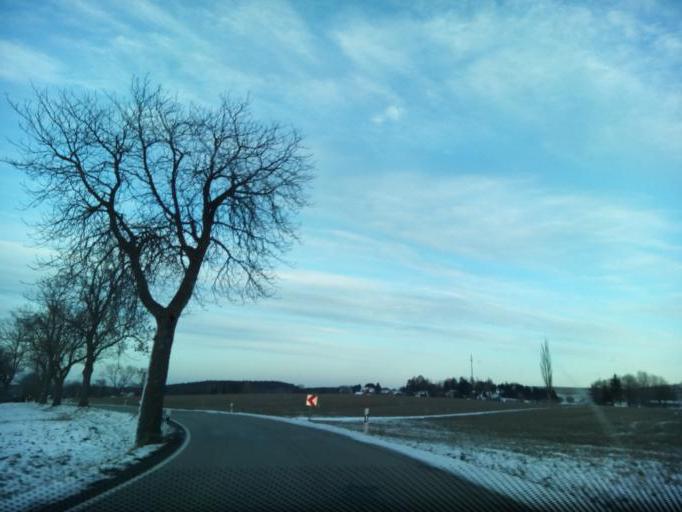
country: DE
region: Saxony
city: Brand-Erbisdorf
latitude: 50.8321
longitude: 13.2907
